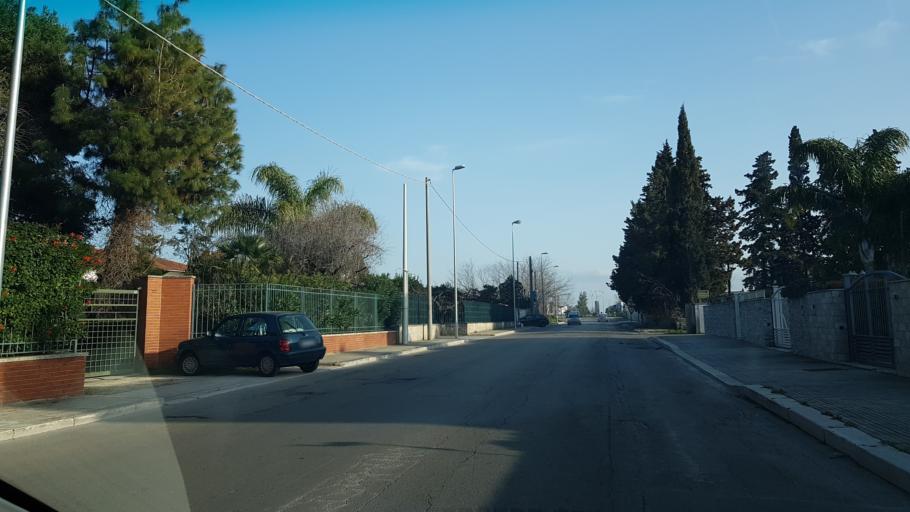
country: IT
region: Apulia
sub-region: Provincia di Lecce
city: Squinzano
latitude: 40.4296
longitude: 18.0515
